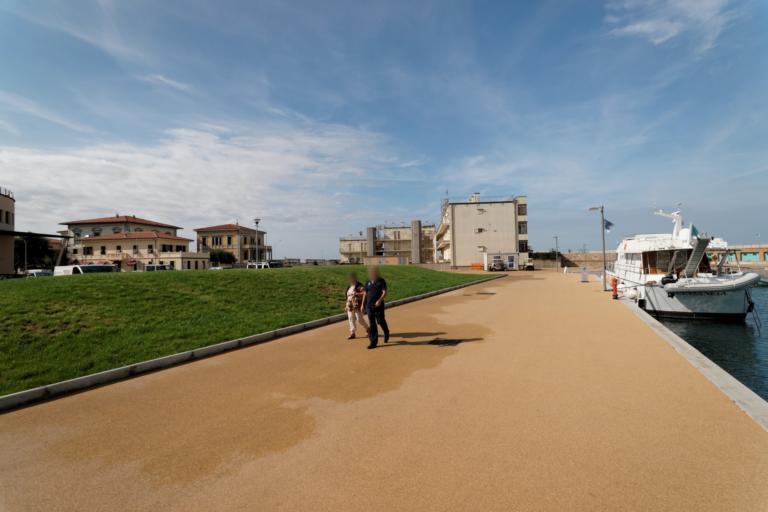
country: IT
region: Tuscany
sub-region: Province of Pisa
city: Marina di Pisa
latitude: 43.6770
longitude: 10.2712
